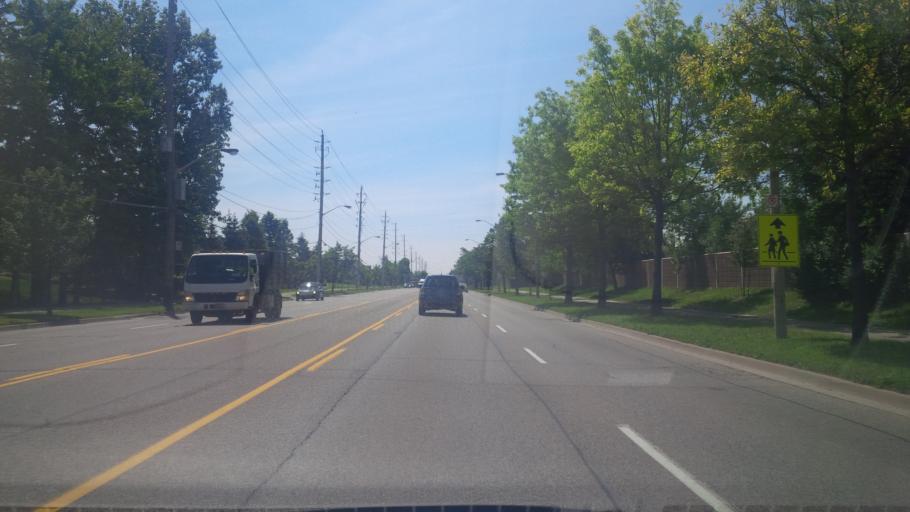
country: CA
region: Ontario
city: Burlington
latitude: 43.3768
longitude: -79.8027
